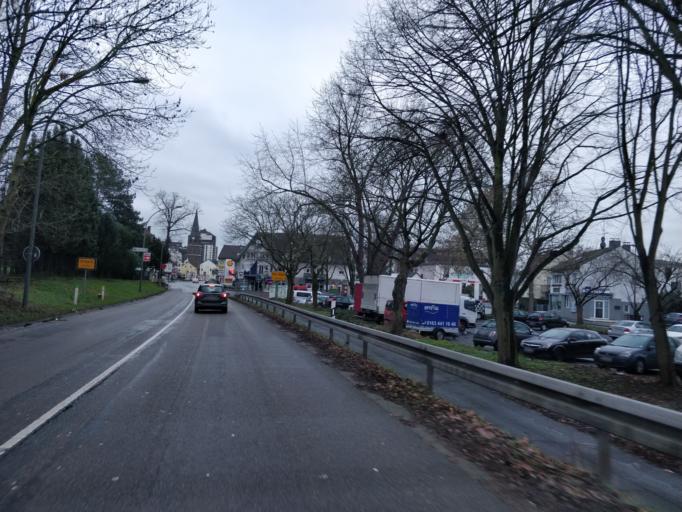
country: DE
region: North Rhine-Westphalia
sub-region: Regierungsbezirk Koln
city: Eil
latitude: 50.8837
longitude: 7.0816
